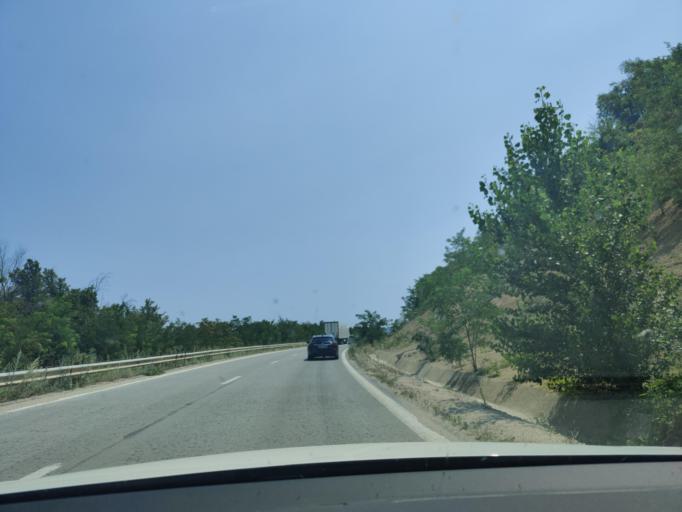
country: BG
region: Montana
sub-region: Obshtina Montana
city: Montana
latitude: 43.4266
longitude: 23.1555
